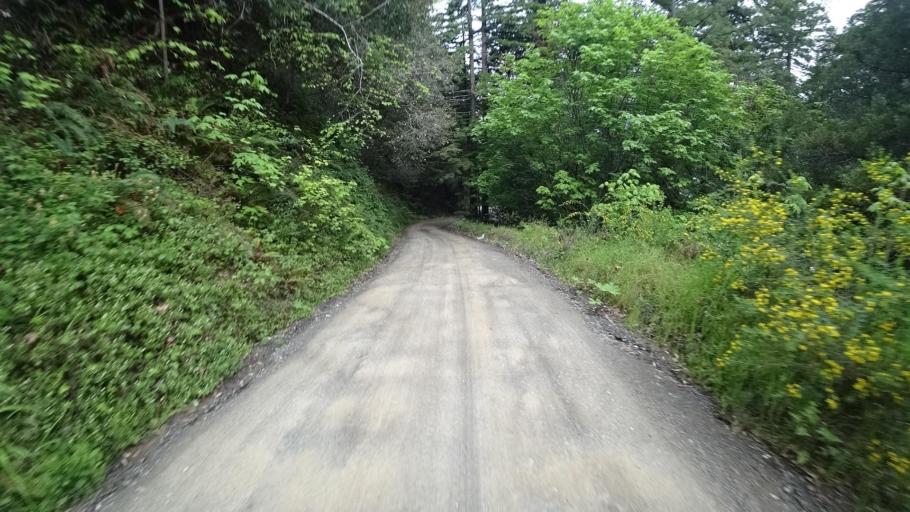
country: US
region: California
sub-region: Humboldt County
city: Redway
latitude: 40.3201
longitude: -123.8317
